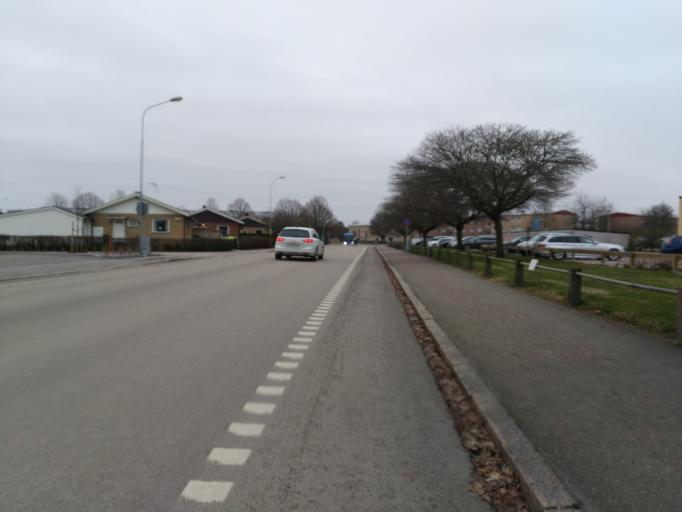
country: SE
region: Vaestra Goetaland
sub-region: Lidkopings Kommun
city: Lidkoping
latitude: 58.4950
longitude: 13.1580
